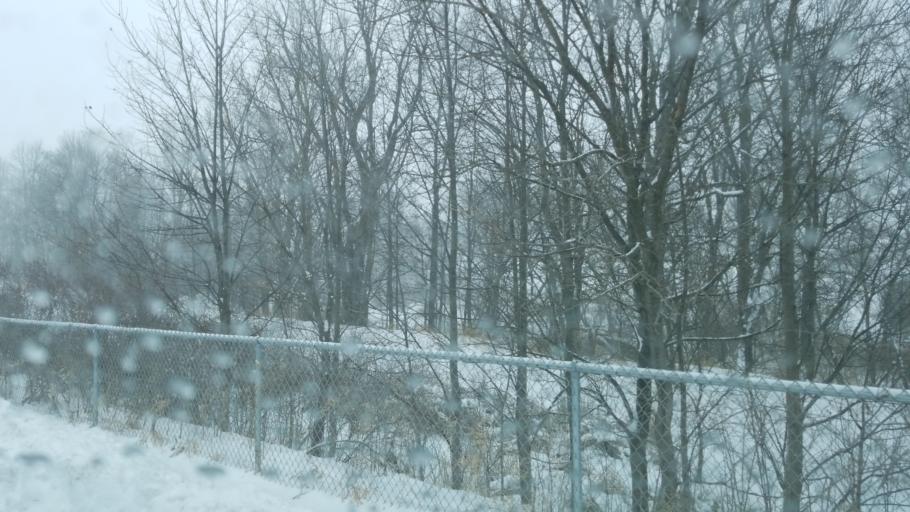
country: US
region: Michigan
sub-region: Osceola County
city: Reed City
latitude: 43.8896
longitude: -85.5237
